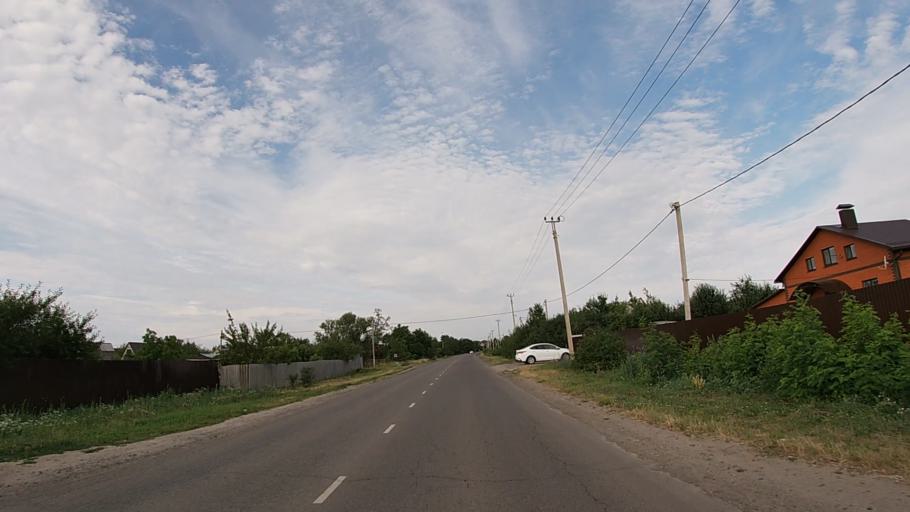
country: RU
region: Belgorod
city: Severnyy
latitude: 50.6969
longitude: 36.5747
